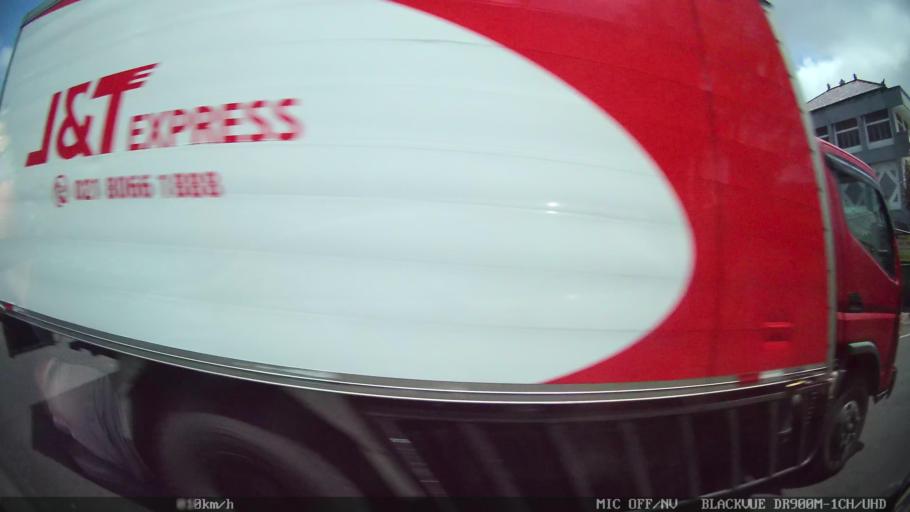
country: ID
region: Bali
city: Banjar Pasekan
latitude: -8.5982
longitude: 115.2828
